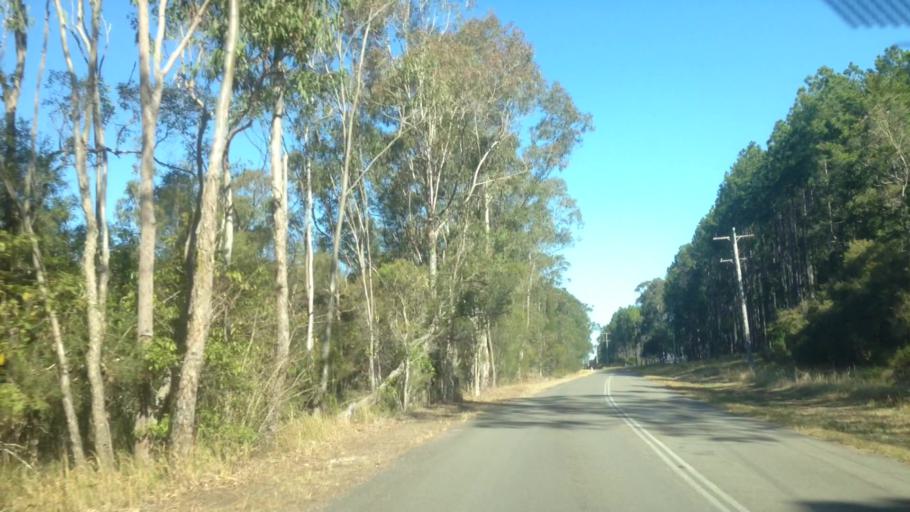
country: AU
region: New South Wales
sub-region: Lake Macquarie Shire
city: Cooranbong
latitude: -33.0979
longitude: 151.4533
